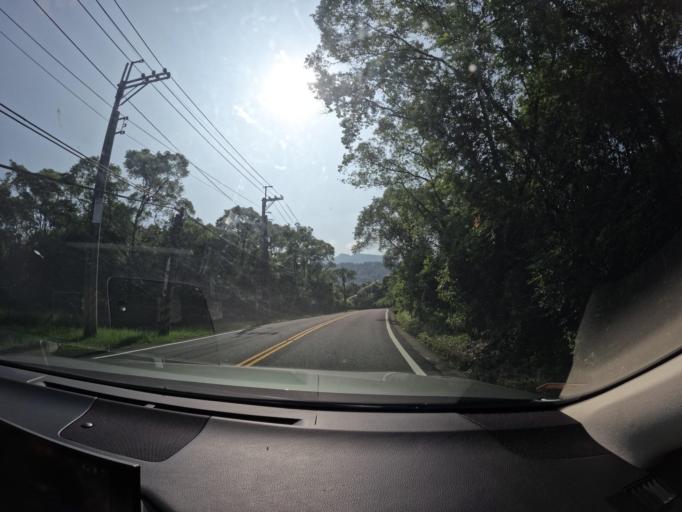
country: TW
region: Taiwan
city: Yujing
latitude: 23.0619
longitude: 120.5662
